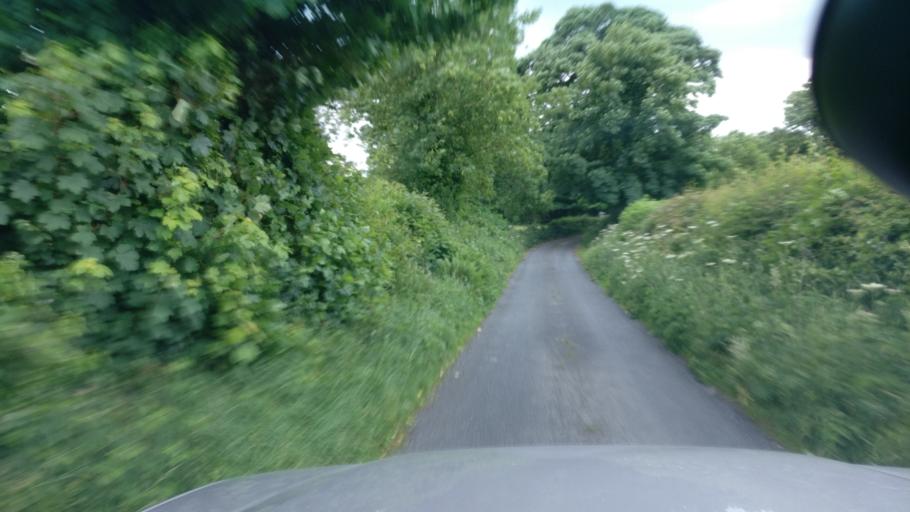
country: IE
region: Connaught
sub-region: County Galway
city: Ballinasloe
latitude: 53.3067
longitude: -8.2757
